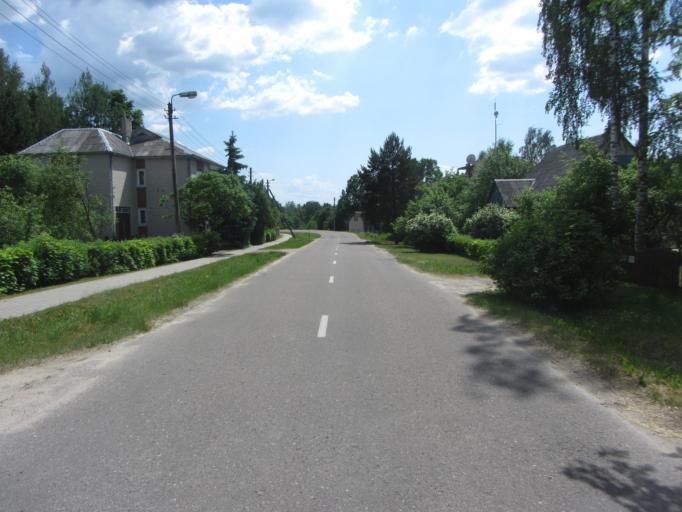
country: LT
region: Kauno apskritis
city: Jonava
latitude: 55.0416
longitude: 24.2573
